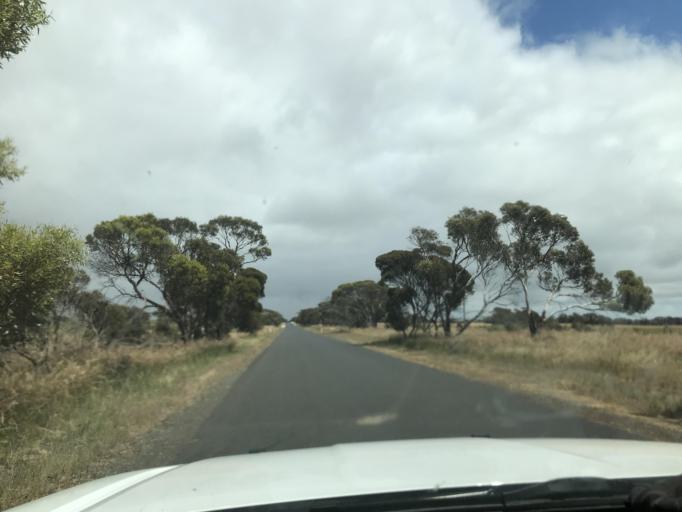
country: AU
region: South Australia
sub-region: Tatiara
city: Bordertown
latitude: -36.1223
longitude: 141.0784
